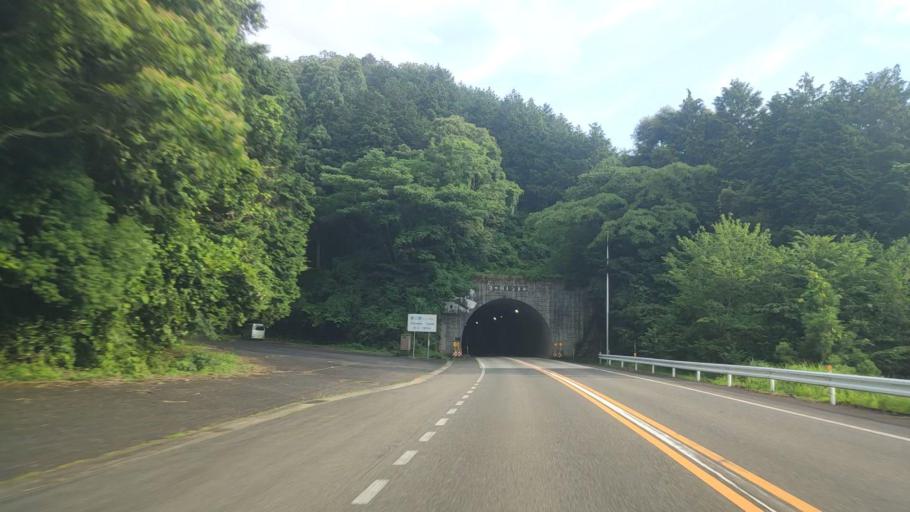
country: JP
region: Tottori
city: Kurayoshi
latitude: 35.3457
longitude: 133.7487
